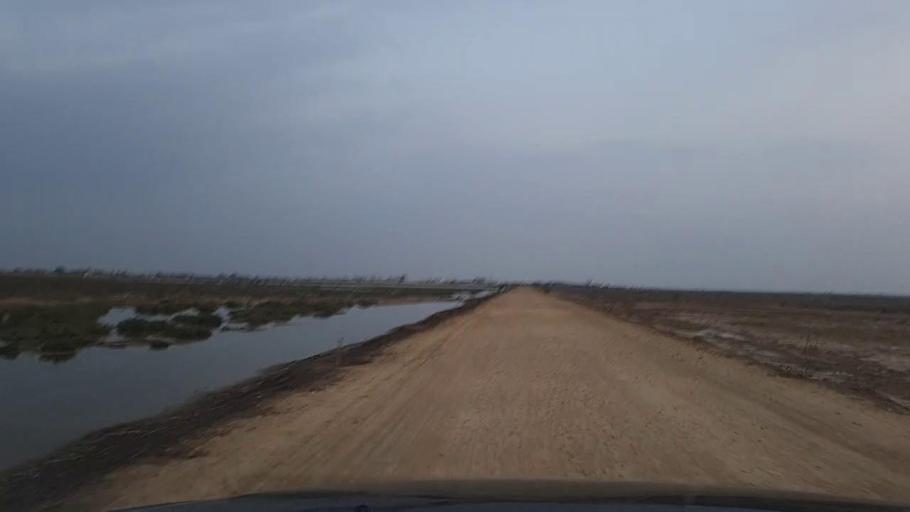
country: PK
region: Sindh
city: Jati
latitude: 24.4956
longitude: 68.3865
